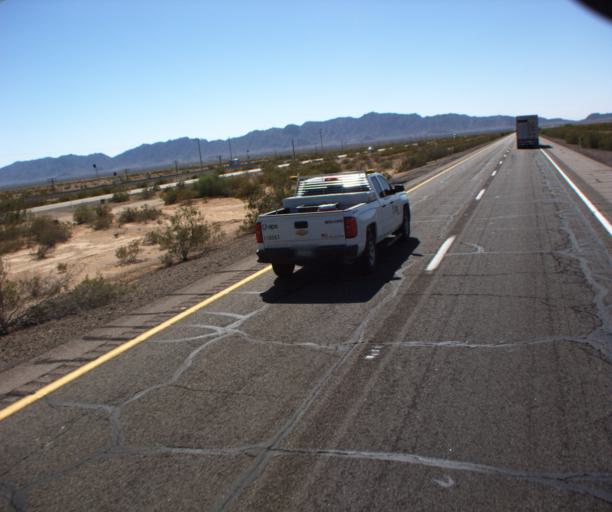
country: US
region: Arizona
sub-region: Yuma County
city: Wellton
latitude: 32.7615
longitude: -113.6342
